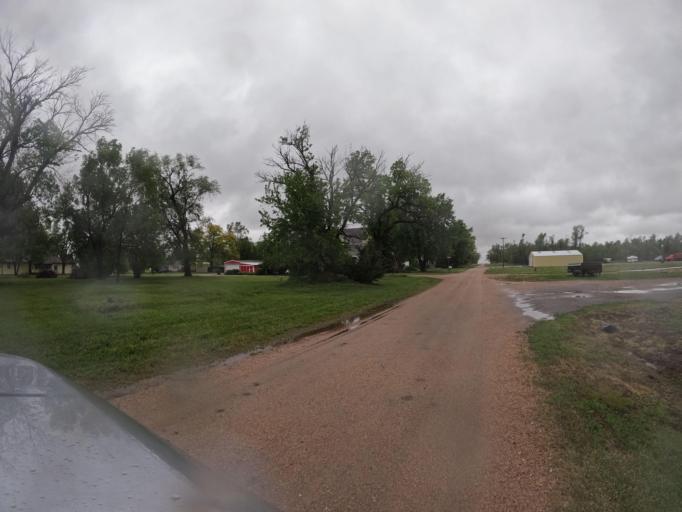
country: US
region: Nebraska
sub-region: Clay County
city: Harvard
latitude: 40.6147
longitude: -98.0985
